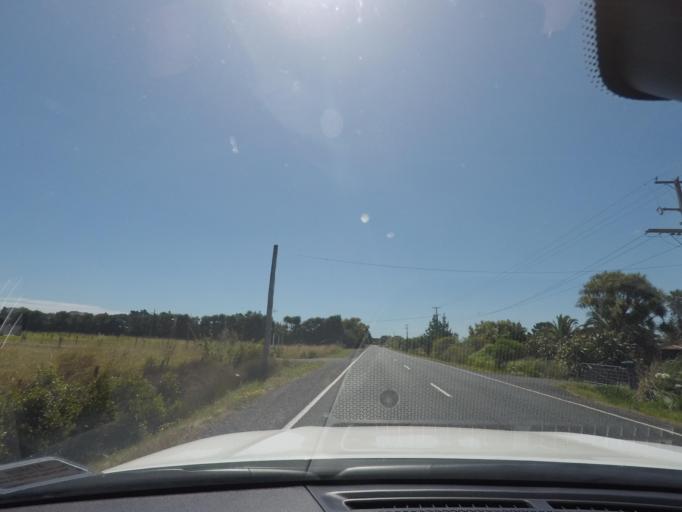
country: NZ
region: Auckland
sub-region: Auckland
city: Parakai
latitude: -36.6404
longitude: 174.3905
